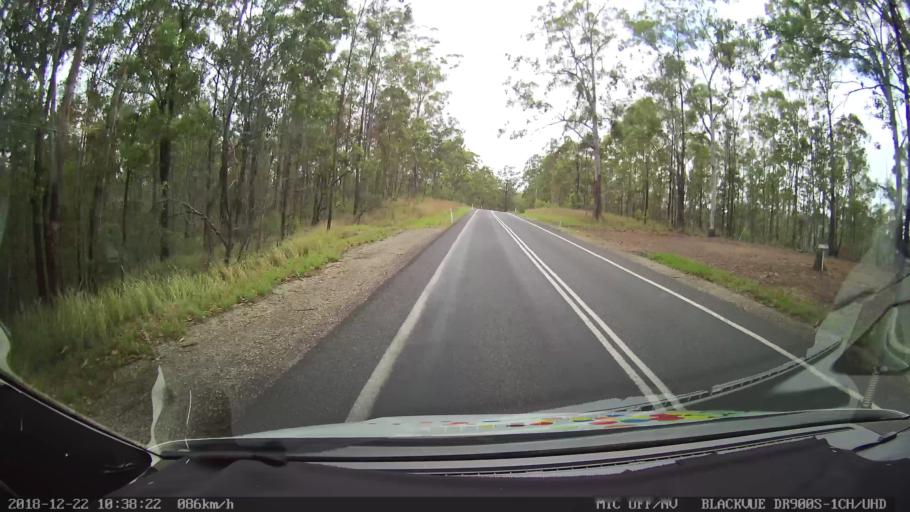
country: AU
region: New South Wales
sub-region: Clarence Valley
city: South Grafton
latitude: -29.6321
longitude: 152.7187
